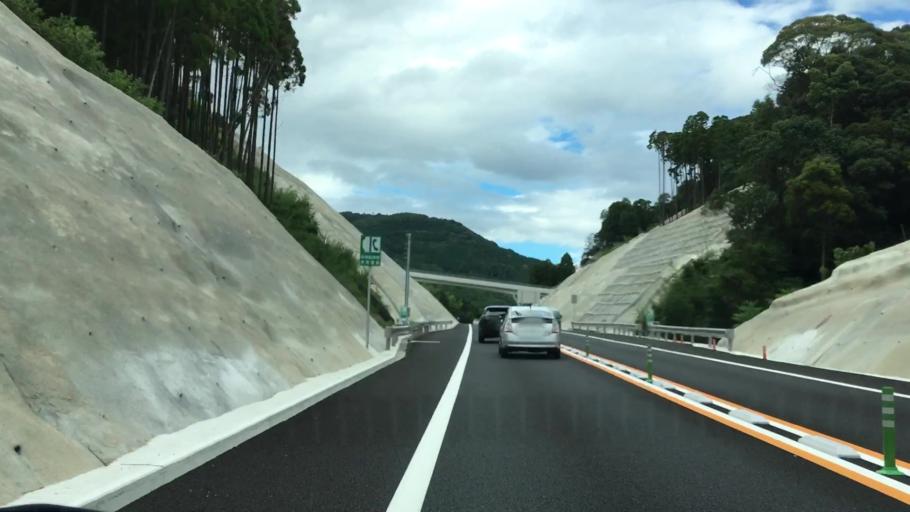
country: JP
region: Saga Prefecture
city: Imaricho-ko
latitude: 33.3047
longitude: 129.9159
